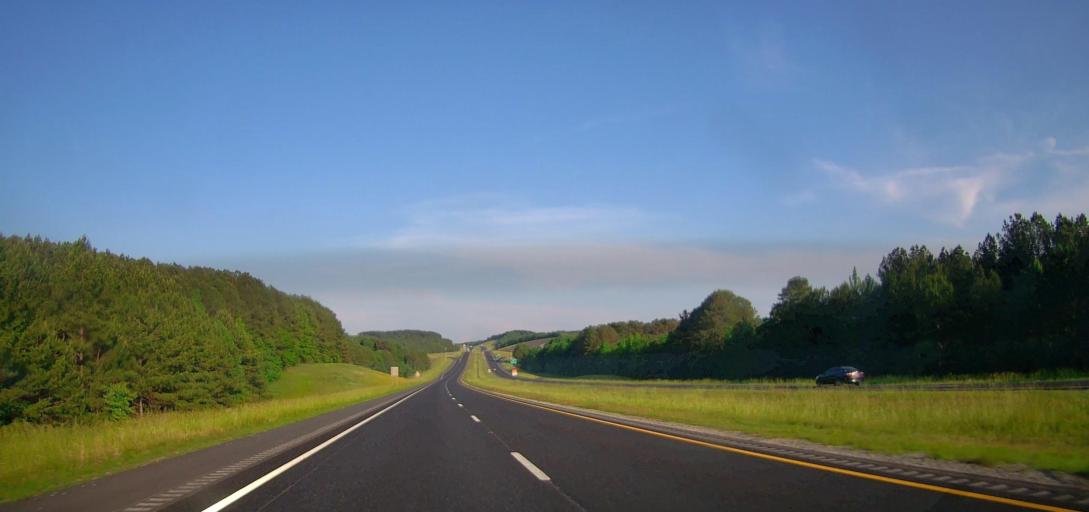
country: US
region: Alabama
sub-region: Marion County
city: Guin
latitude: 34.0183
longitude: -87.8423
